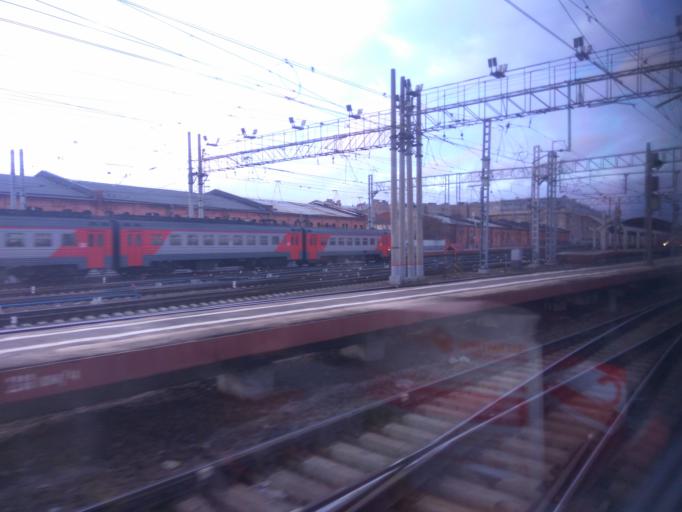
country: RU
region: St.-Petersburg
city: Centralniy
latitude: 59.9235
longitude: 30.3645
